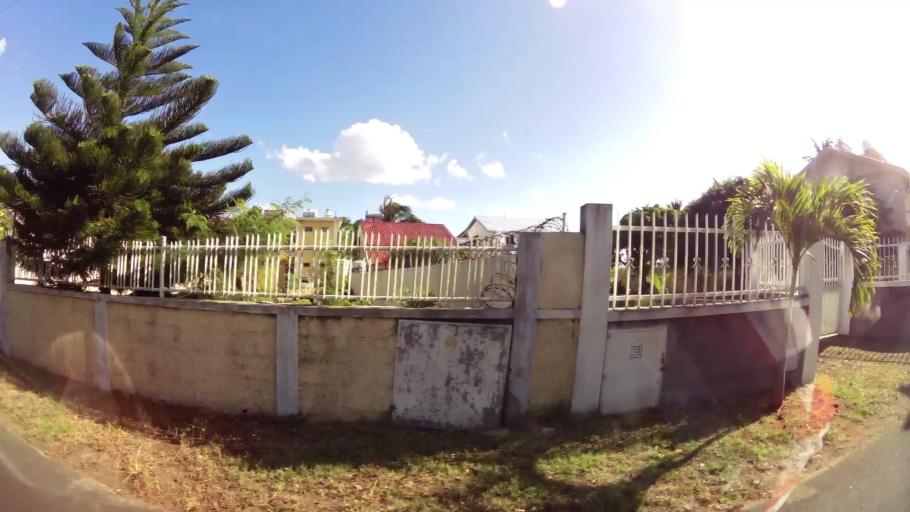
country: MU
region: Black River
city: Albion
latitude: -20.2052
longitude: 57.4054
